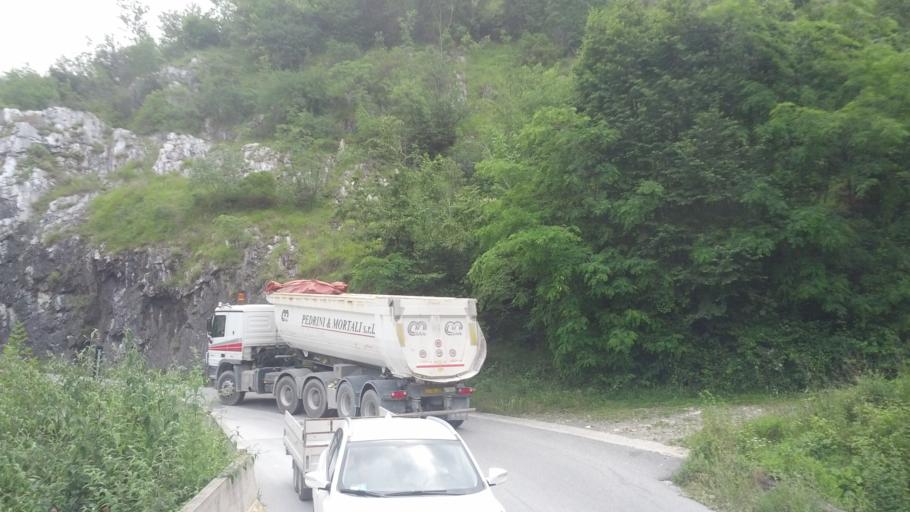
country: IT
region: Tuscany
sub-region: Provincia di Massa-Carrara
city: Massa
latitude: 44.0777
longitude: 10.1347
